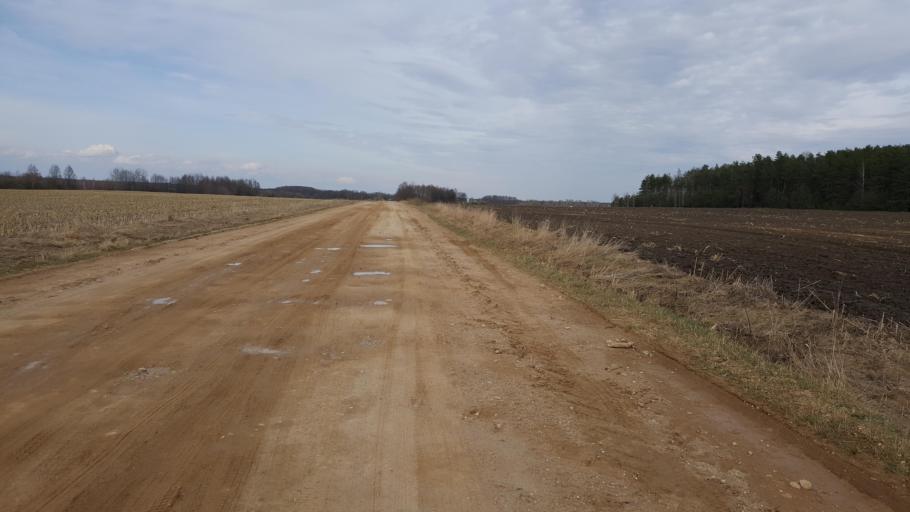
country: BY
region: Brest
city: Zhabinka
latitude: 52.3812
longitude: 23.9930
